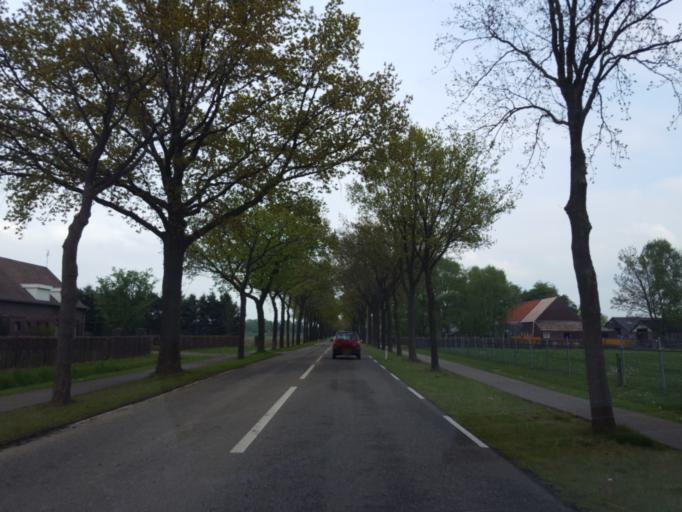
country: NL
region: Limburg
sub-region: Gemeente Weert
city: Weert
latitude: 51.2570
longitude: 5.6575
